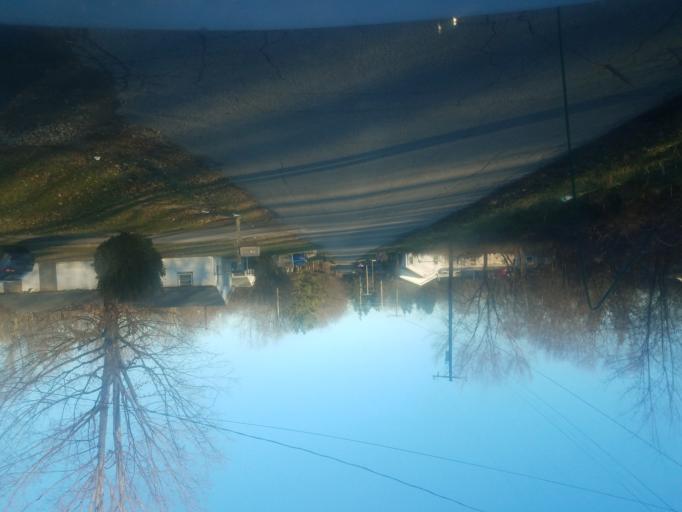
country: US
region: Ohio
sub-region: Richland County
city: Mansfield
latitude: 40.7885
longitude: -82.5449
